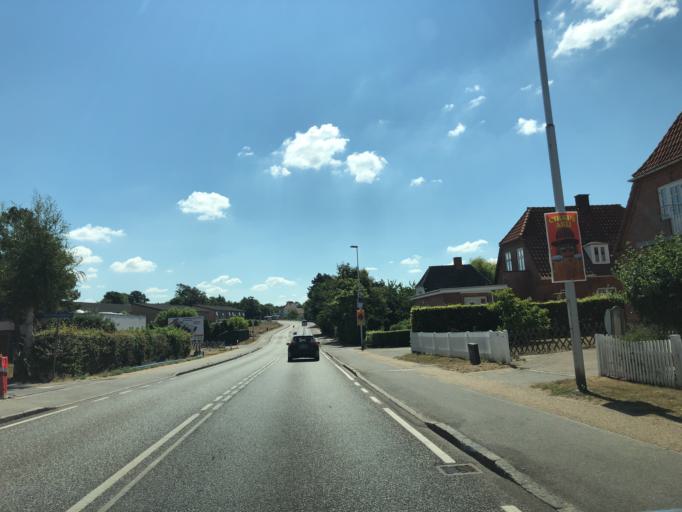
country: DK
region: Capital Region
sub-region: Halsnaes Kommune
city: Hundested
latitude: 55.9656
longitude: 11.8554
